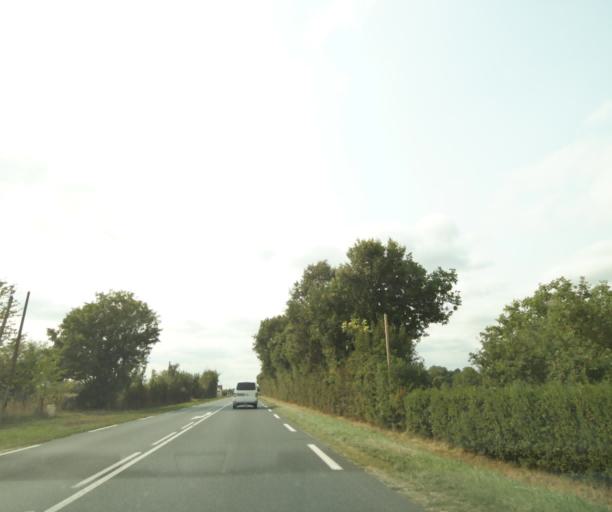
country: FR
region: Centre
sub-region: Departement de l'Indre
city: Chatillon-sur-Indre
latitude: 46.9719
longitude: 1.1914
